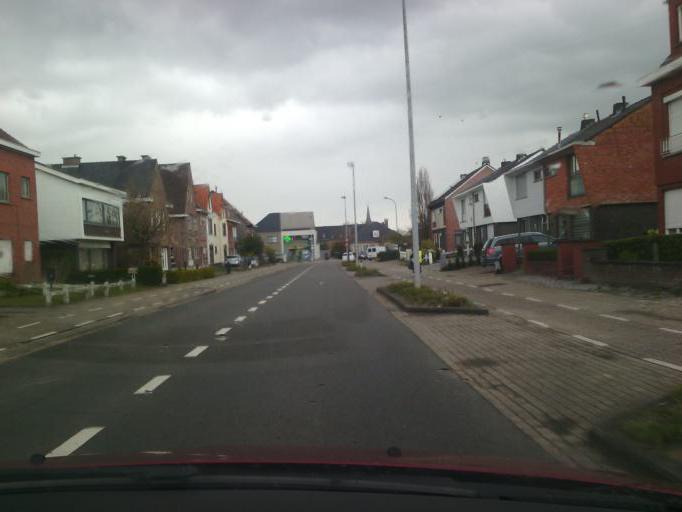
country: BE
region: Flanders
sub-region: Provincie Oost-Vlaanderen
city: Sint-Niklaas
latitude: 51.1474
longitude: 4.1472
